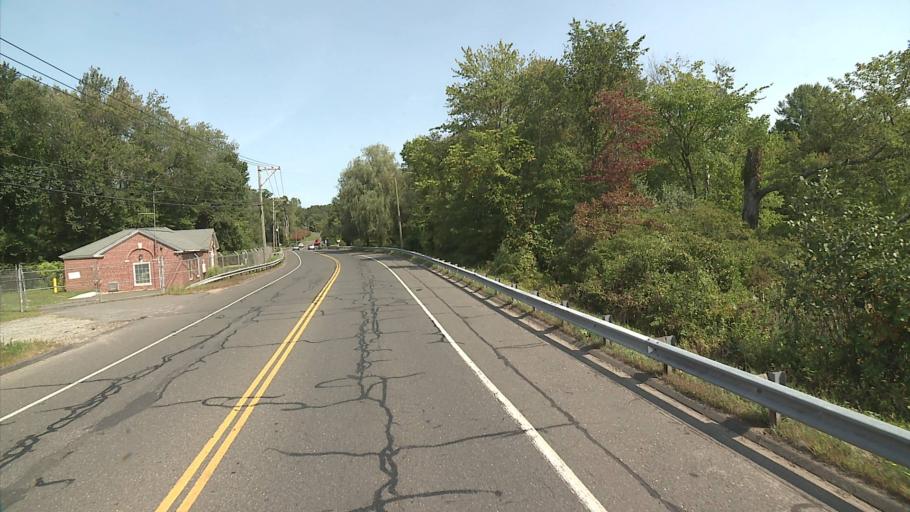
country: US
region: Connecticut
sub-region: Fairfield County
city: Newtown
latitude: 41.4061
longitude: -73.2734
